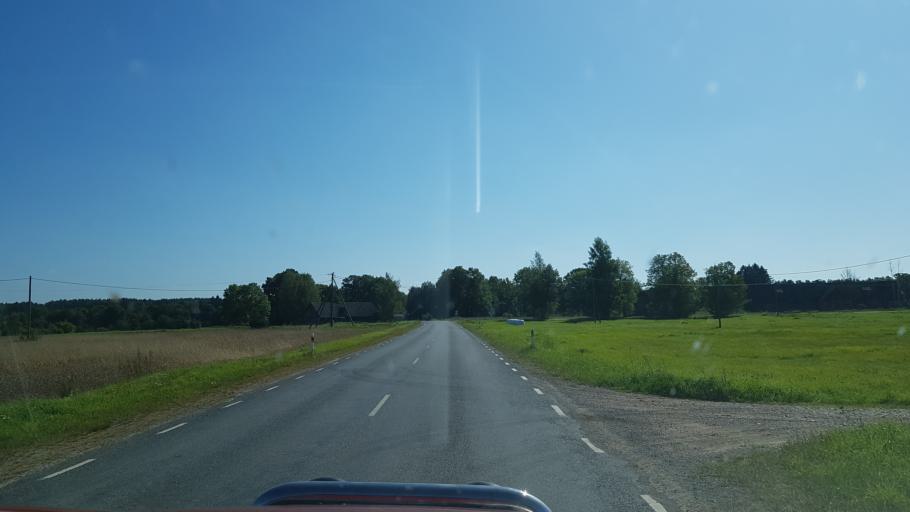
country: EE
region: Polvamaa
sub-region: Polva linn
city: Polva
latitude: 58.2709
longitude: 27.1249
